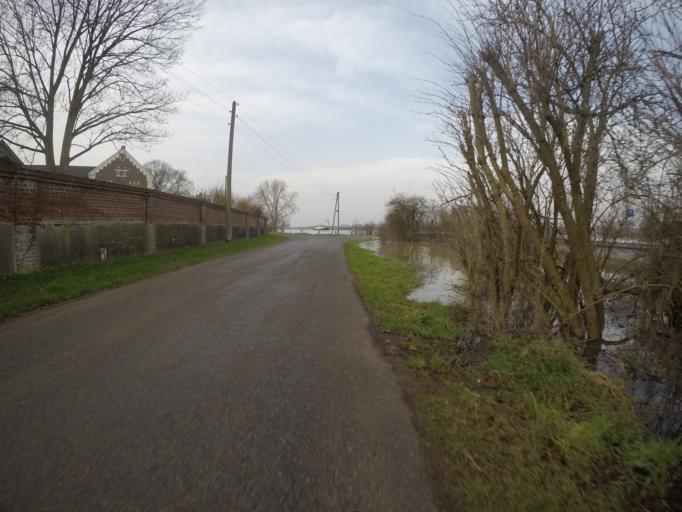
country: DE
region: North Rhine-Westphalia
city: Rees
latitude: 51.7513
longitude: 6.3959
